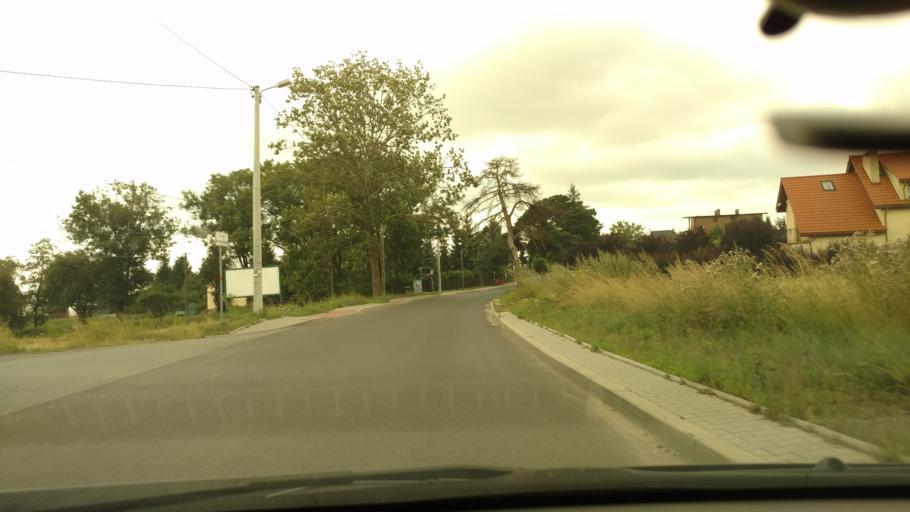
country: PL
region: Lesser Poland Voivodeship
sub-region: Powiat krakowski
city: Zielonki
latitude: 50.1236
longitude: 19.9395
